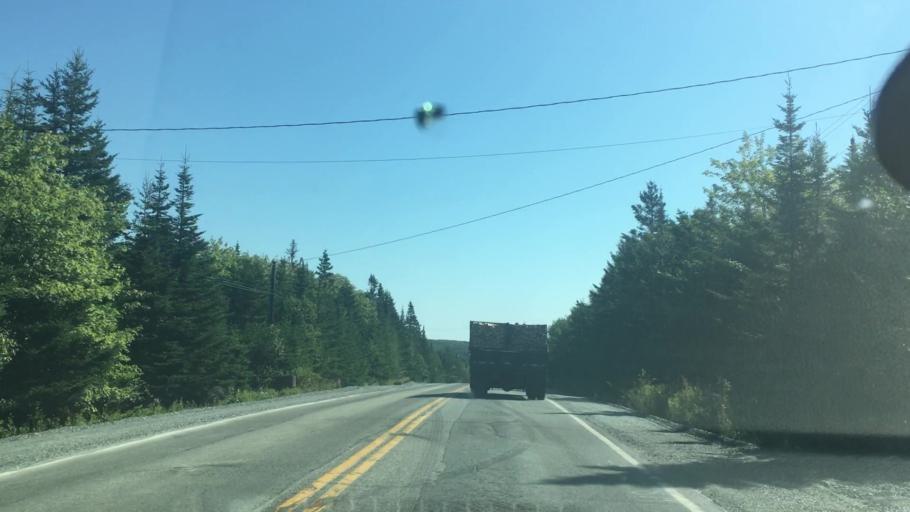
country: CA
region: Nova Scotia
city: New Glasgow
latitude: 44.9047
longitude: -62.4686
